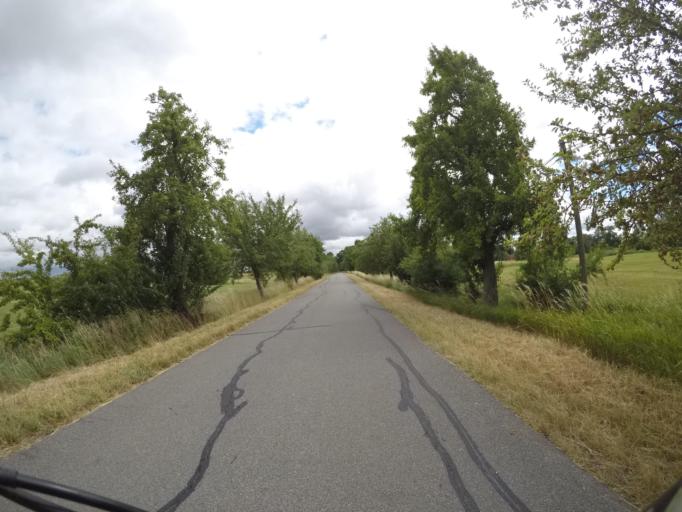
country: DE
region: Lower Saxony
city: Dannenberg
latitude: 53.1492
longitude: 11.1022
